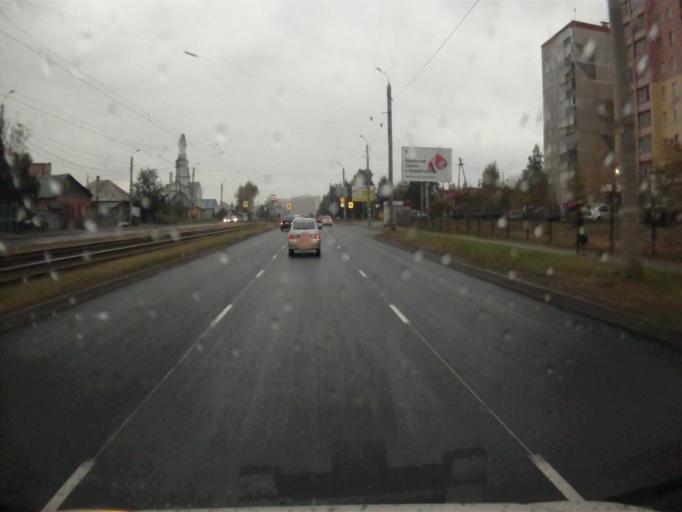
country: RU
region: Chelyabinsk
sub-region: Gorod Chelyabinsk
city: Chelyabinsk
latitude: 55.1845
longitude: 61.3696
